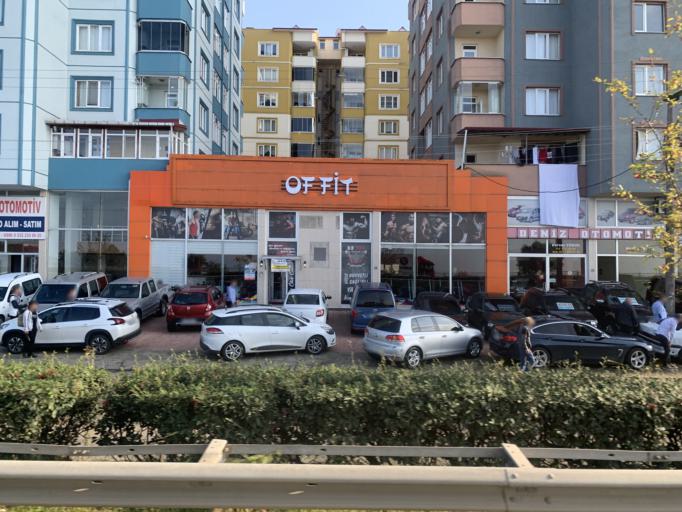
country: TR
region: Trabzon
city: Of
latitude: 40.9425
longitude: 40.2601
